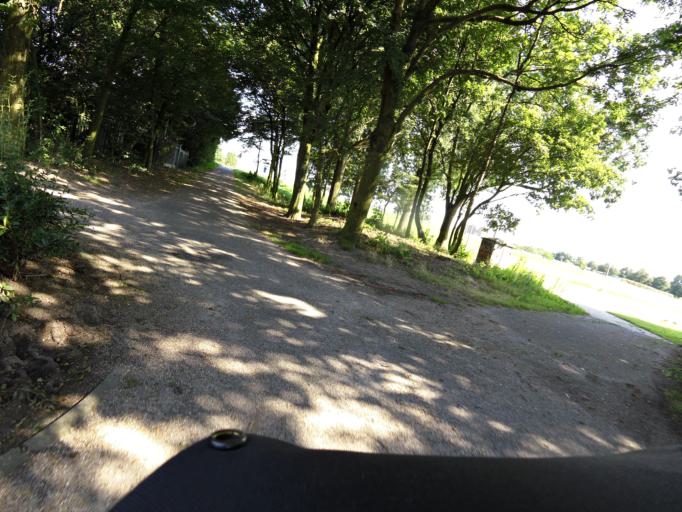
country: NL
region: South Holland
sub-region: Gemeente Oud-Beijerland
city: Oud-Beijerland
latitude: 51.8271
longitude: 4.4260
